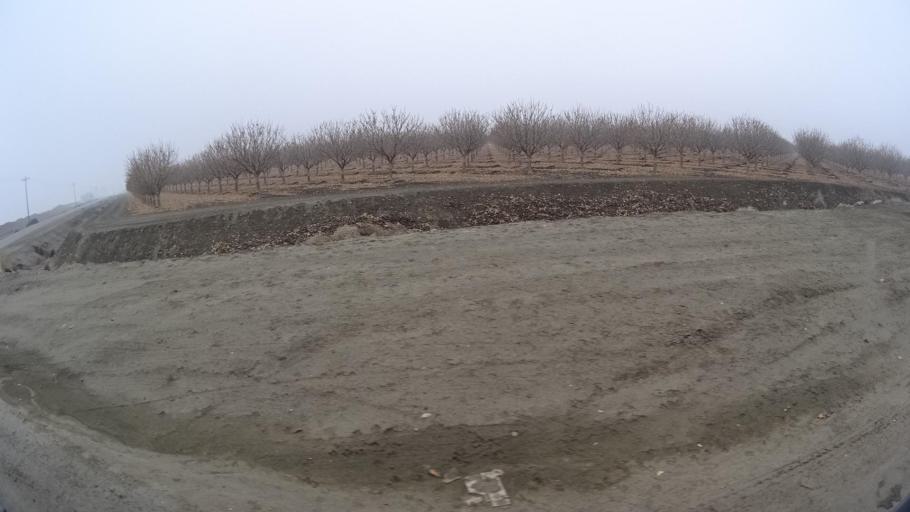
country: US
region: California
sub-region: Kern County
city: Buttonwillow
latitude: 35.4121
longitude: -119.5186
